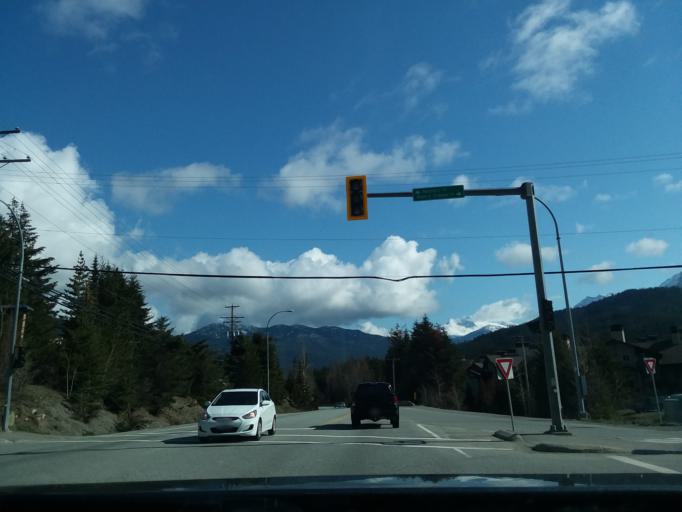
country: CA
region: British Columbia
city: Whistler
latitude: 50.1262
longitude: -122.9561
